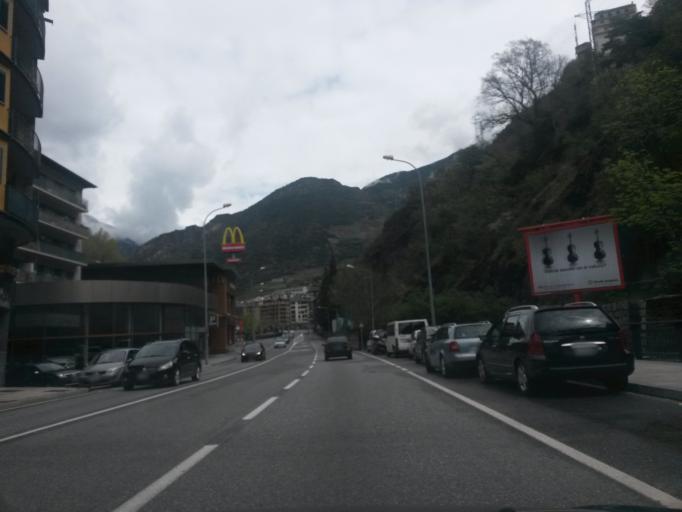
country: AD
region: Sant Julia de Loria
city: Sant Julia de Loria
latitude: 42.4592
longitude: 1.4886
